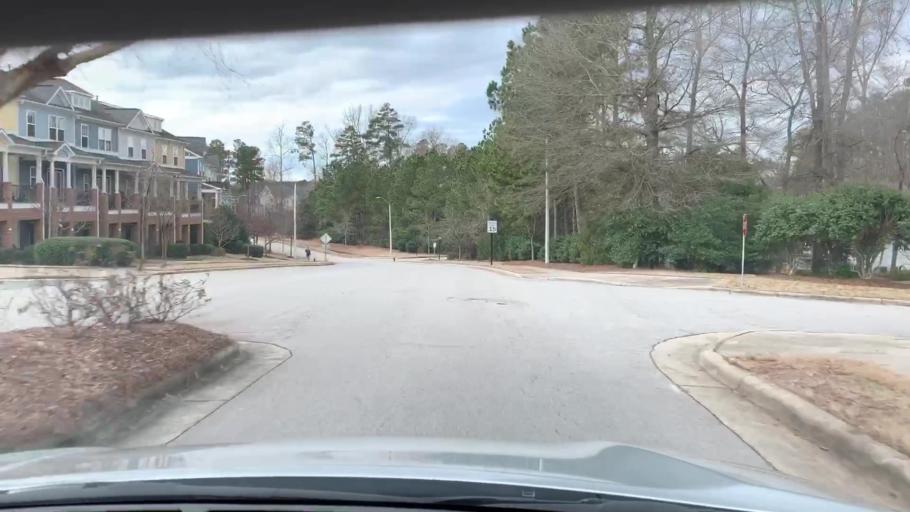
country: US
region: North Carolina
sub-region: Wake County
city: Green Level
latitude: 35.8188
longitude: -78.9030
